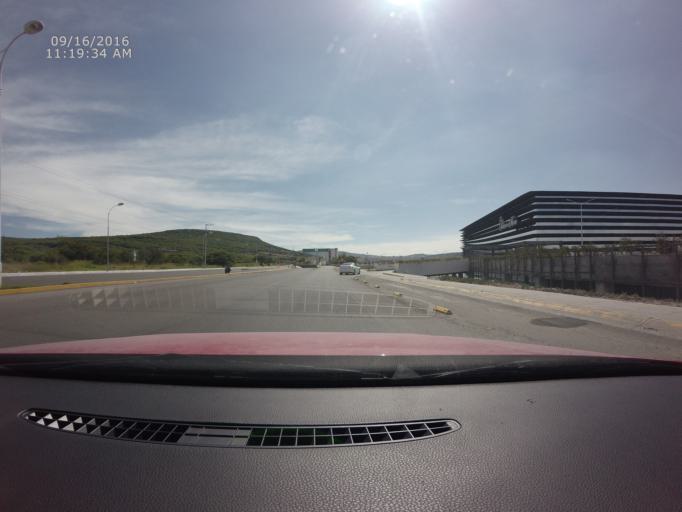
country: MX
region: Queretaro
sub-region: Queretaro
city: El Salitre
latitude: 20.6778
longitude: -100.4373
